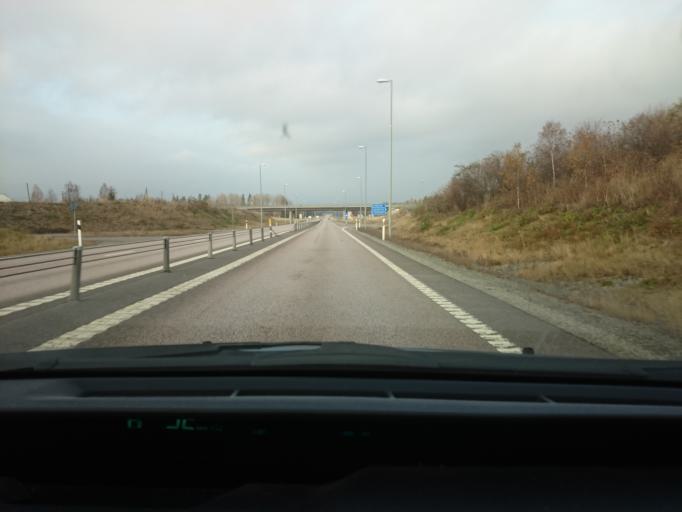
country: SE
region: Vaestmanland
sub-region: Sala Kommun
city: Sala
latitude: 59.9059
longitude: 16.5351
